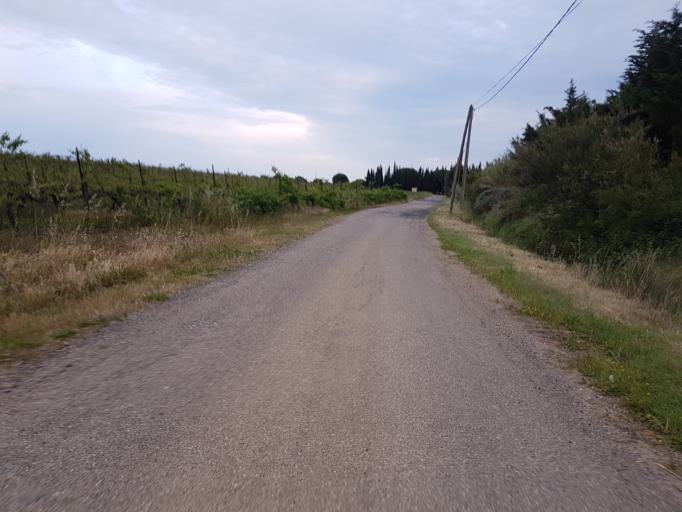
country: FR
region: Languedoc-Roussillon
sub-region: Departement de l'Herault
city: Portiragnes
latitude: 43.3148
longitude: 3.3403
